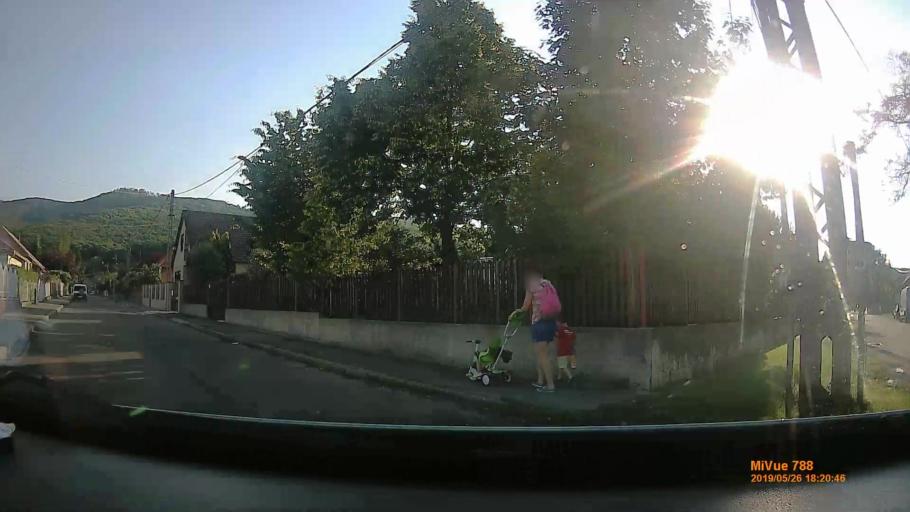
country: HU
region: Borsod-Abauj-Zemplen
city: Sajobabony
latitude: 48.1068
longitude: 20.6757
